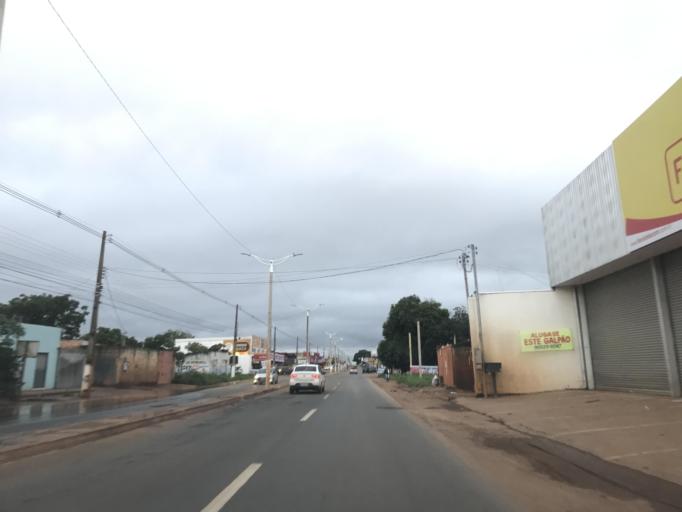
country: BR
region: Goias
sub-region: Luziania
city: Luziania
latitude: -16.2127
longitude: -47.9295
